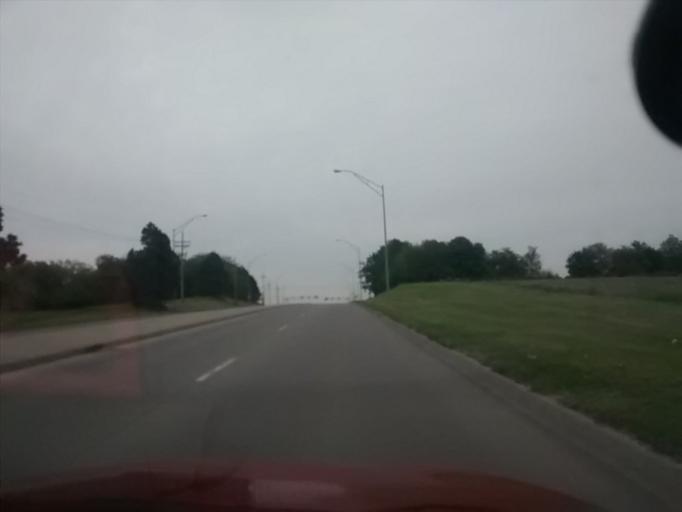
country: US
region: Nebraska
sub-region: Sarpy County
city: Offutt Air Force Base
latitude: 41.1596
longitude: -95.9513
